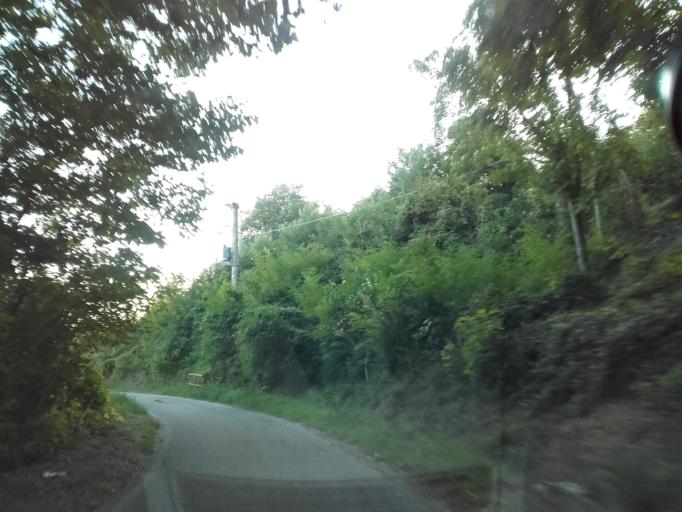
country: IT
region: Piedmont
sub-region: Provincia di Asti
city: Mongardino
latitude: 44.8616
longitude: 8.2138
